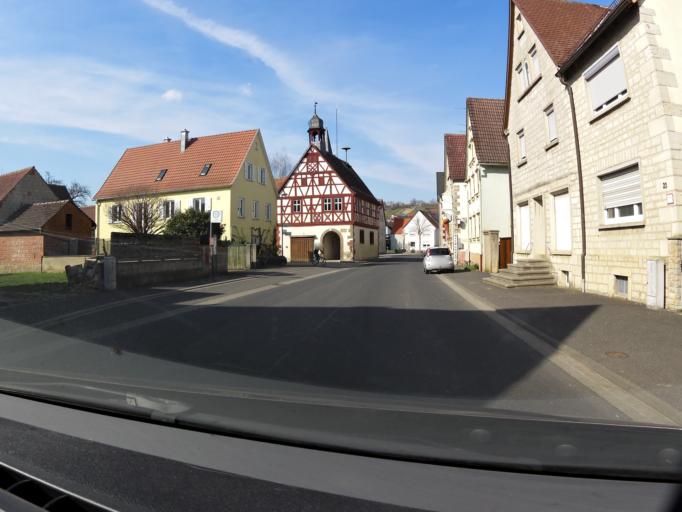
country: DE
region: Bavaria
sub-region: Regierungsbezirk Unterfranken
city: Bieberehren
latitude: 49.5152
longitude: 10.0079
